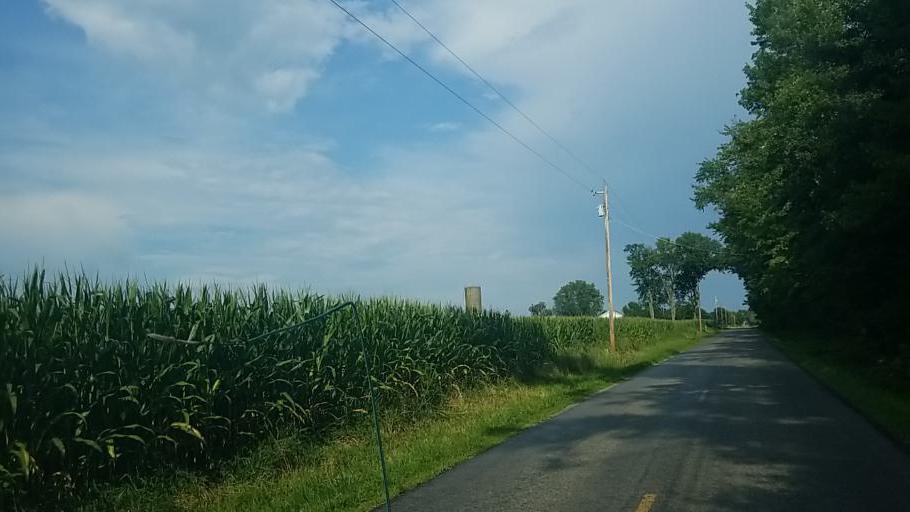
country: US
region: Ohio
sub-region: Wayne County
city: Creston
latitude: 40.9156
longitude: -81.9298
